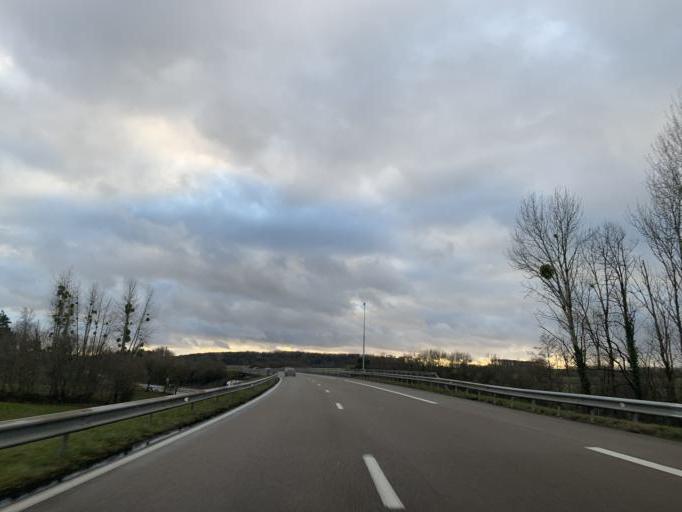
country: FR
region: Champagne-Ardenne
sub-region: Departement de la Haute-Marne
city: Rolampont
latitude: 47.9162
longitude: 5.2222
